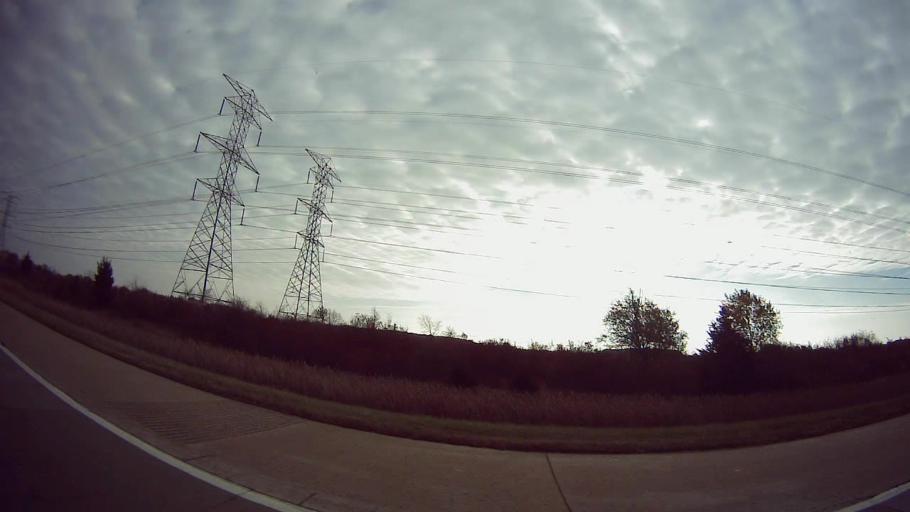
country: US
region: Michigan
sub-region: Monroe County
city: South Rockwood
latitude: 42.0343
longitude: -83.2896
